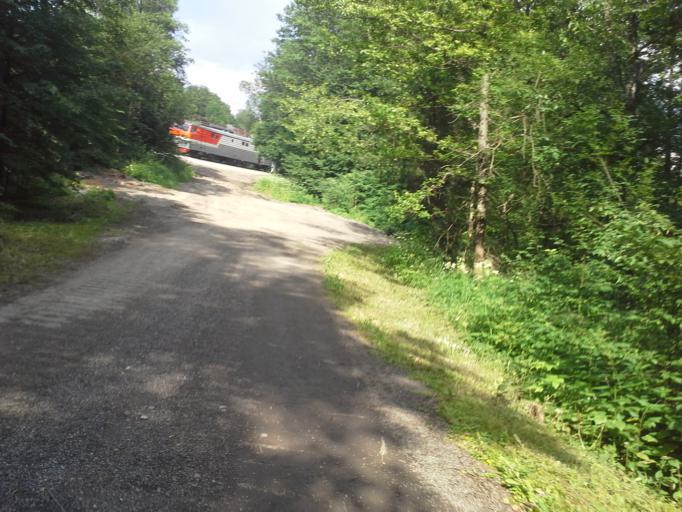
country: RU
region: Moskovskaya
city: Kievskij
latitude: 55.4396
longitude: 36.8441
